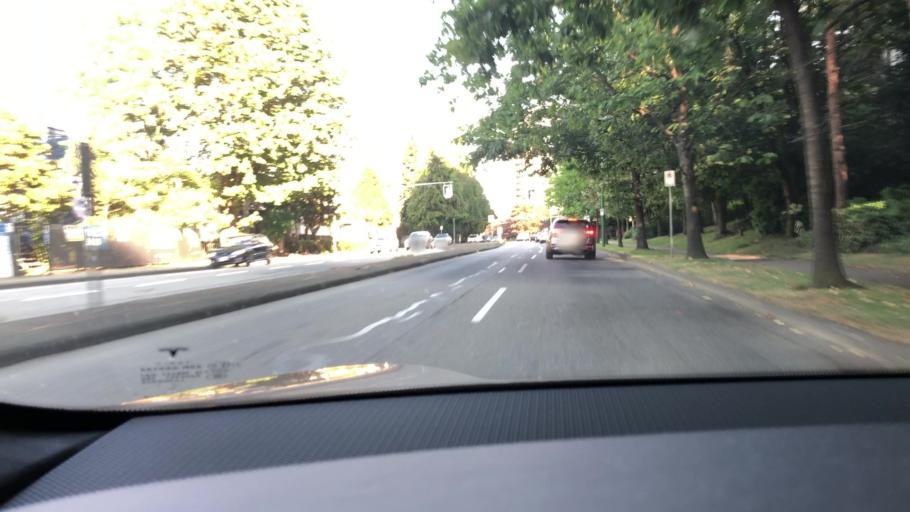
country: CA
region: British Columbia
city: Burnaby
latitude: 49.2307
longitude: -123.0008
